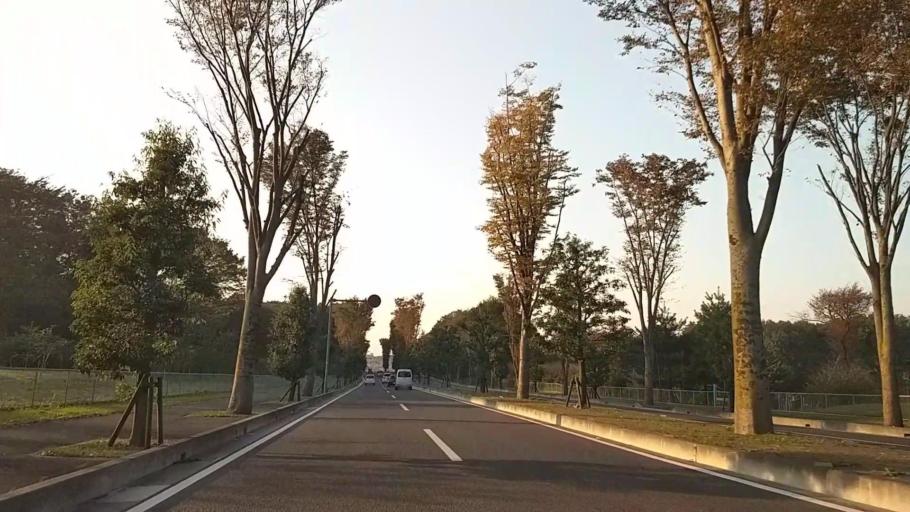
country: JP
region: Saitama
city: Sayama
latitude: 35.8424
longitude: 139.4544
